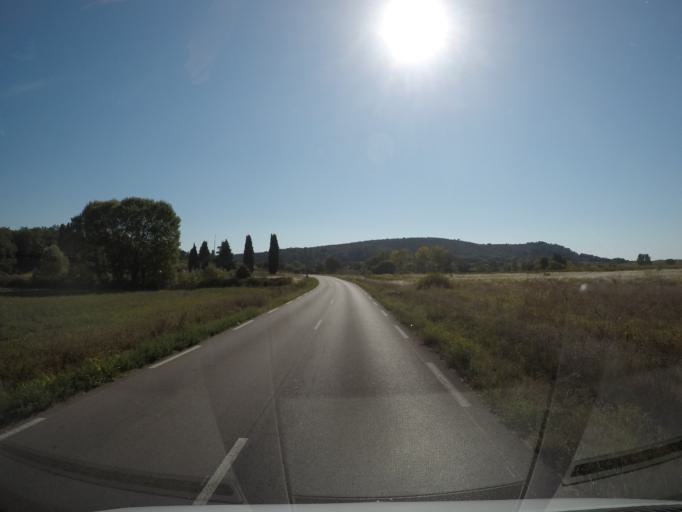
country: FR
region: Languedoc-Roussillon
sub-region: Departement du Gard
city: Ledignan
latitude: 44.0076
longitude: 4.1221
